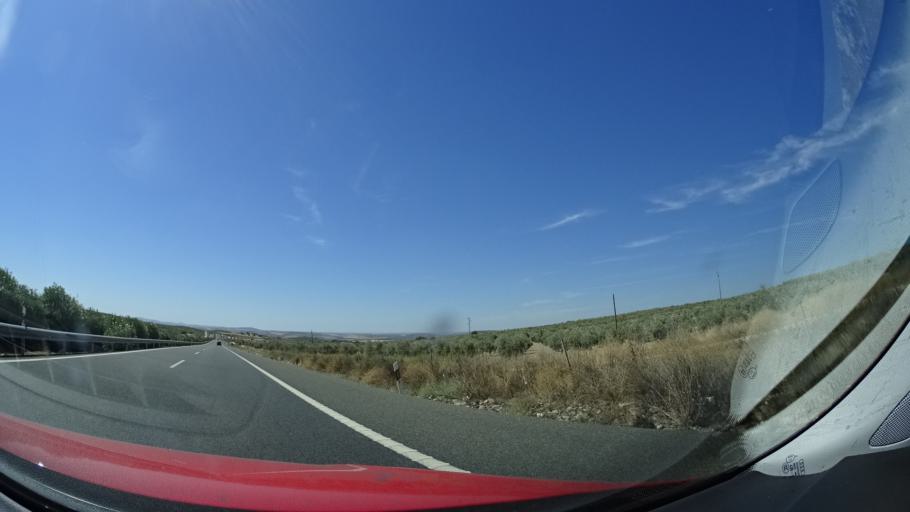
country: ES
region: Andalusia
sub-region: Provincia de Sevilla
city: Gilena
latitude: 37.2797
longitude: -4.9262
